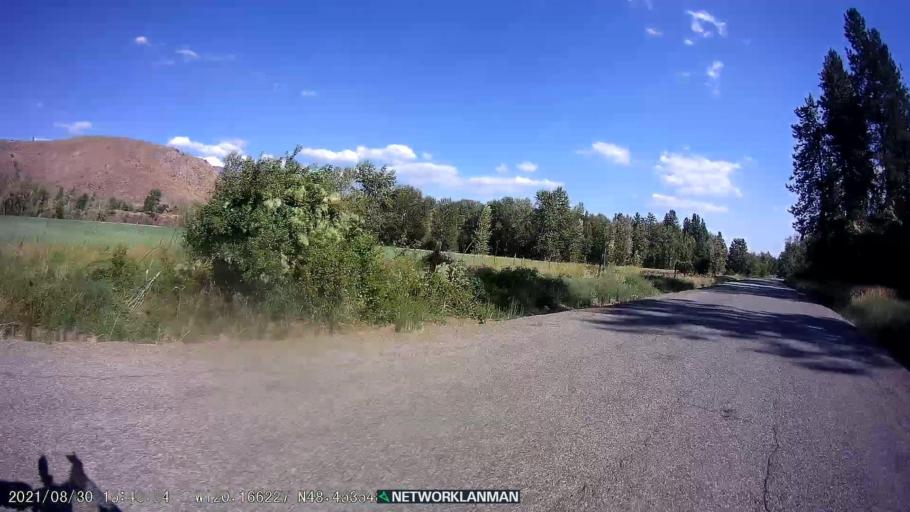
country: US
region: Washington
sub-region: Okanogan County
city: Brewster
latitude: 48.4533
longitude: -120.1660
